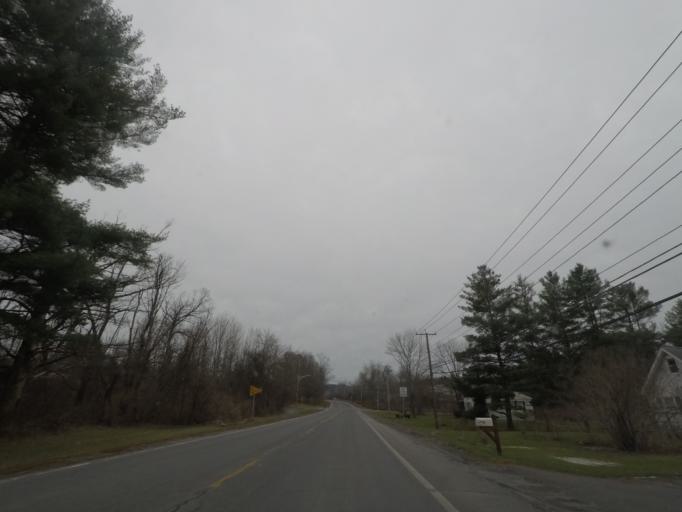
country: US
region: Massachusetts
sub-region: Berkshire County
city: Williamstown
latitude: 42.6794
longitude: -73.2341
